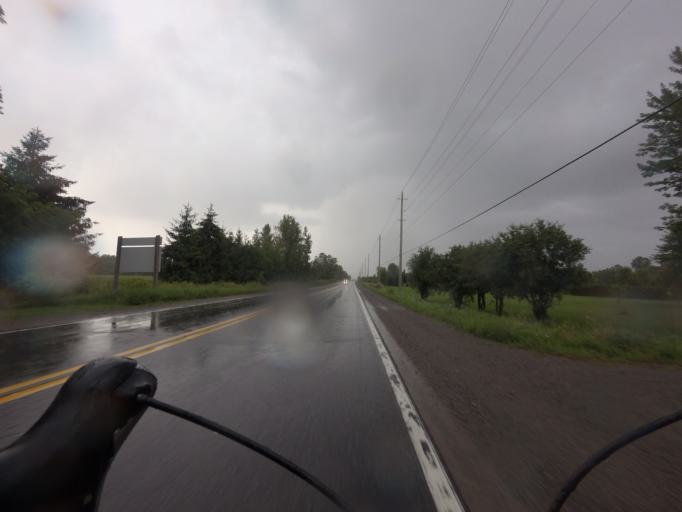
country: CA
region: Ontario
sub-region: Lanark County
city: Smiths Falls
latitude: 44.9539
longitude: -75.8230
